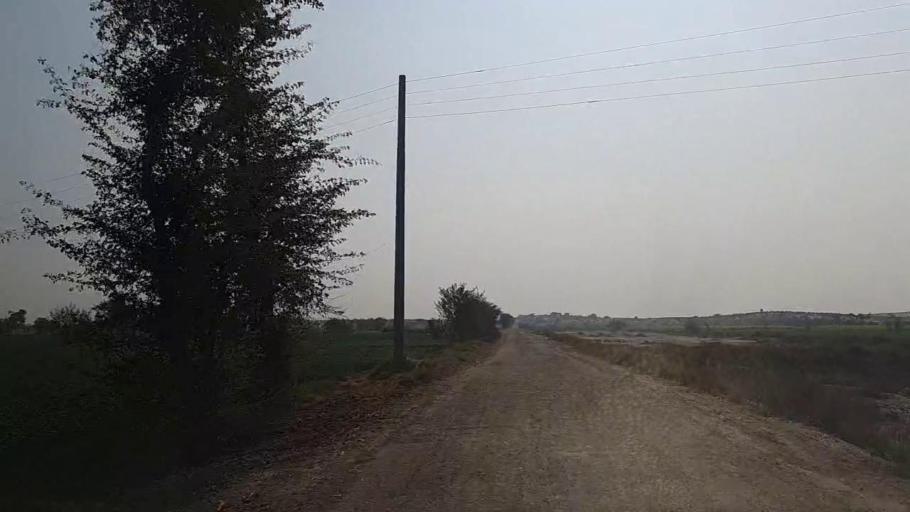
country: PK
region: Sindh
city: Jam Sahib
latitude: 26.4514
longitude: 68.5234
